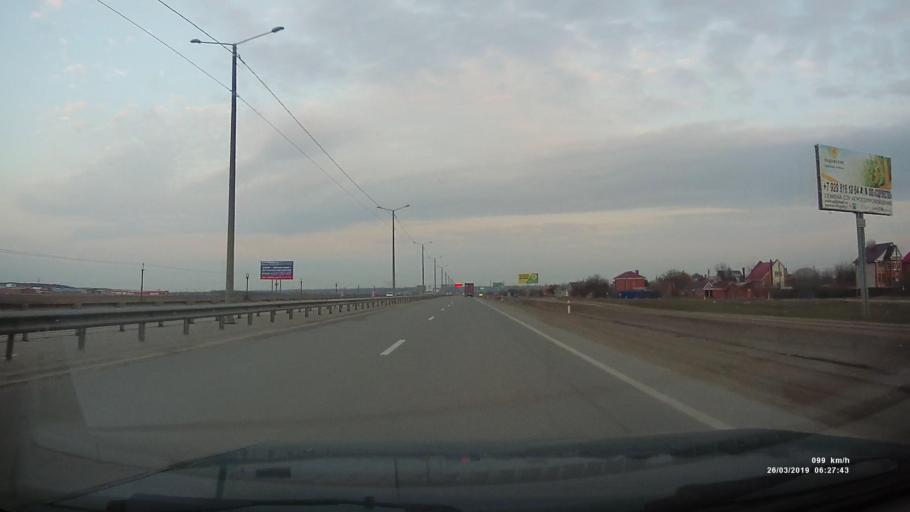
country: RU
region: Rostov
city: Kalinin
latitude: 47.2625
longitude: 39.6085
